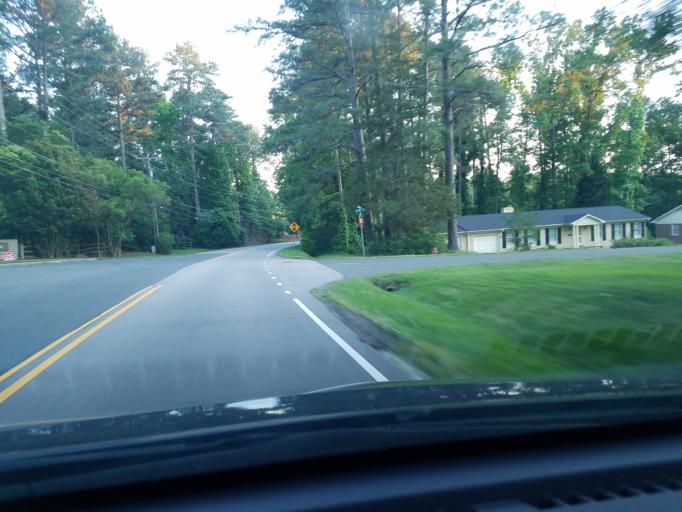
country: US
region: North Carolina
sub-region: Durham County
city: Durham
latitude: 35.9602
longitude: -78.9329
